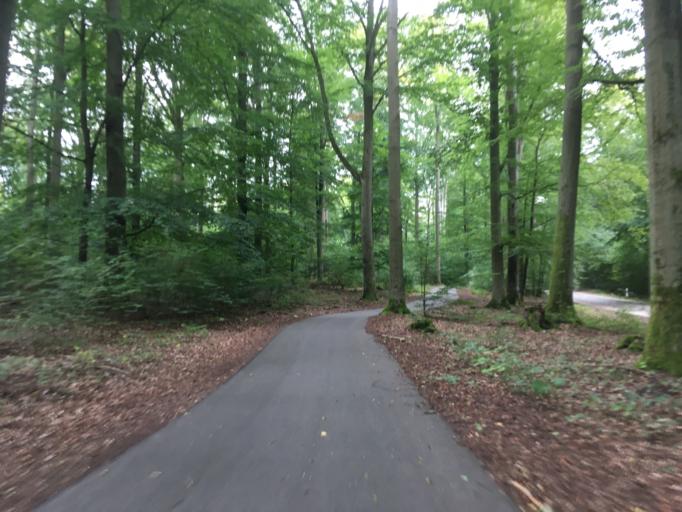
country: DE
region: Brandenburg
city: Friedrichswalde
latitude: 53.0387
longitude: 13.6739
